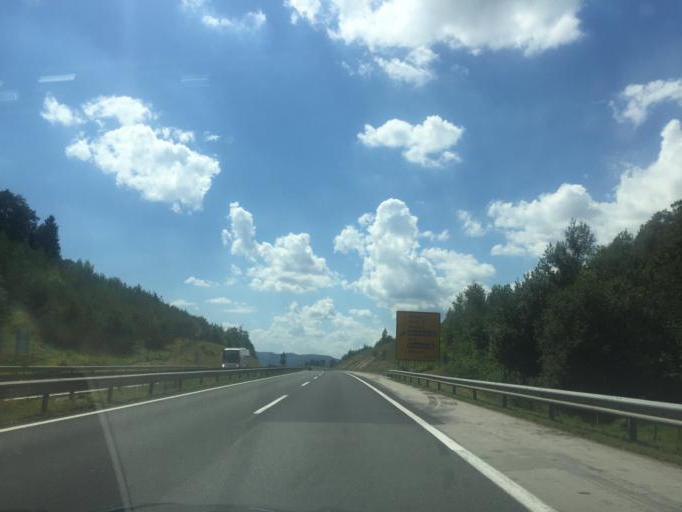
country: SI
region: Domzale
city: Dob
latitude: 46.1548
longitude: 14.6595
